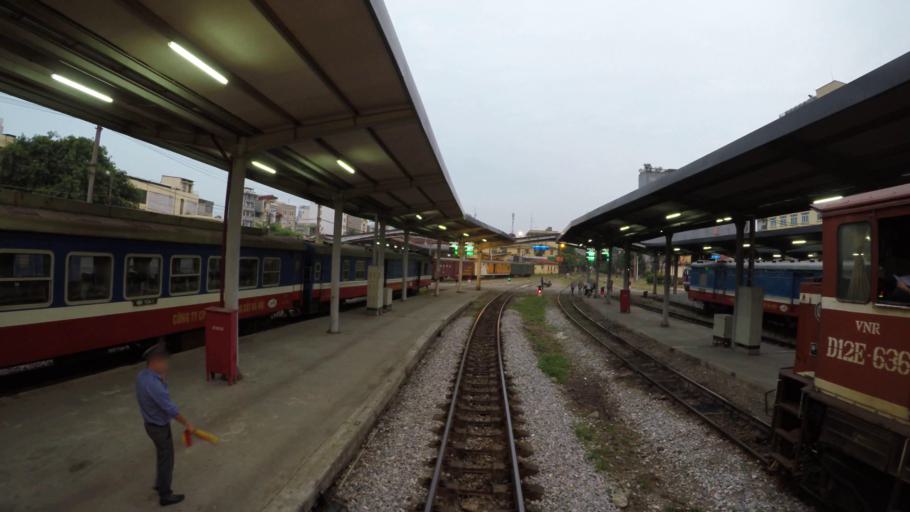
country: VN
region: Ha Noi
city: Hanoi
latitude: 21.0260
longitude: 105.8409
